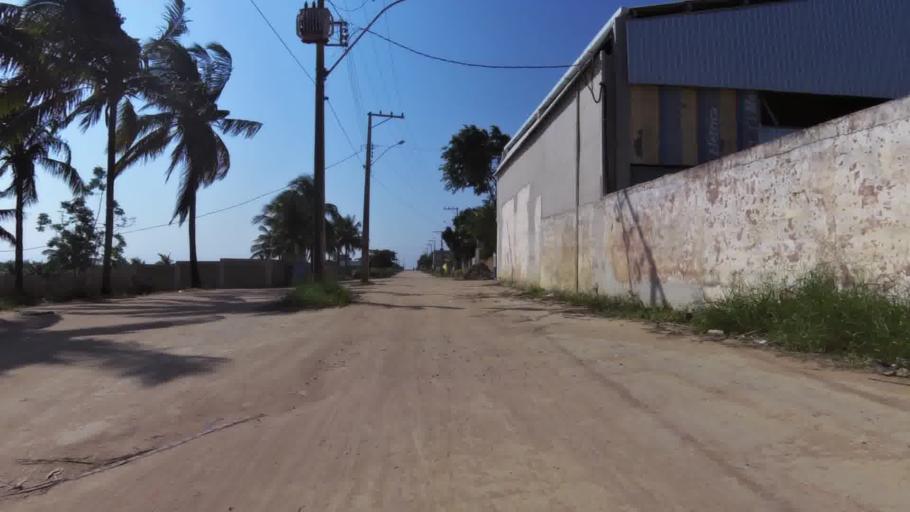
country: BR
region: Espirito Santo
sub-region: Marataizes
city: Marataizes
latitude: -21.0456
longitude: -40.8435
